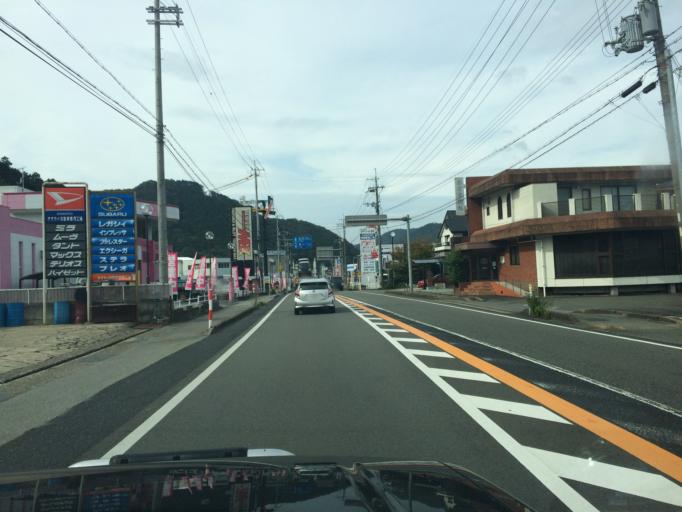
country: JP
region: Hyogo
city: Toyooka
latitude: 35.3443
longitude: 134.8402
